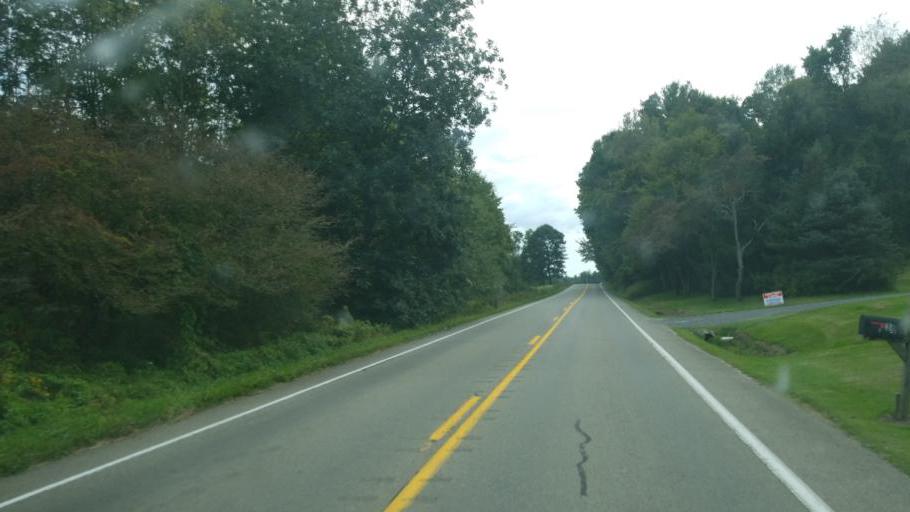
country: US
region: Pennsylvania
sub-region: Mercer County
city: Greenville
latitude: 41.4562
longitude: -80.3671
